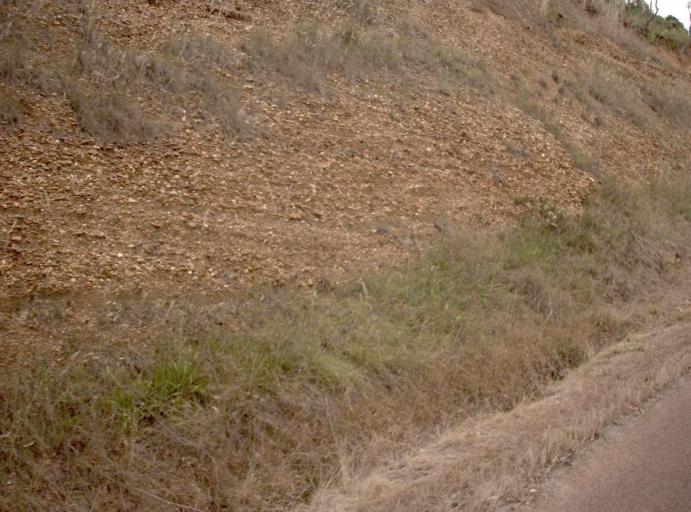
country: AU
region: Victoria
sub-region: East Gippsland
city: Bairnsdale
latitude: -37.8916
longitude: 147.6589
